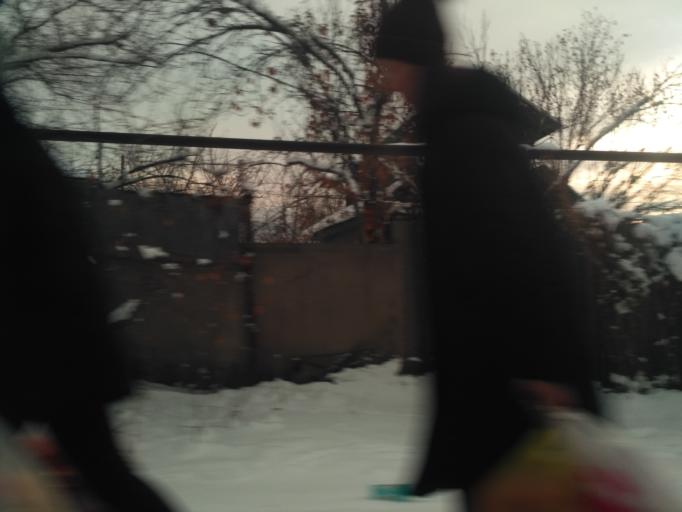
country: KZ
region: Almaty Qalasy
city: Almaty
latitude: 43.2123
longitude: 76.7760
